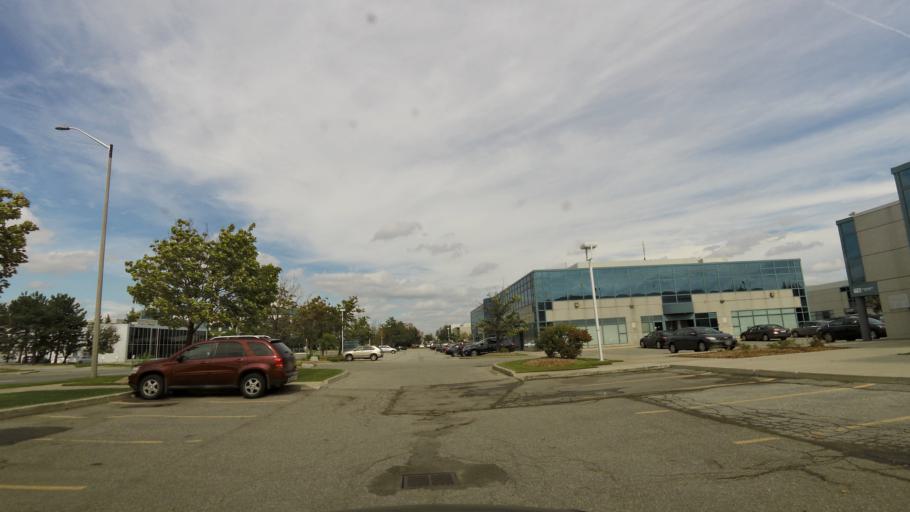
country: CA
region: Ontario
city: Etobicoke
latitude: 43.6593
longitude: -79.6018
